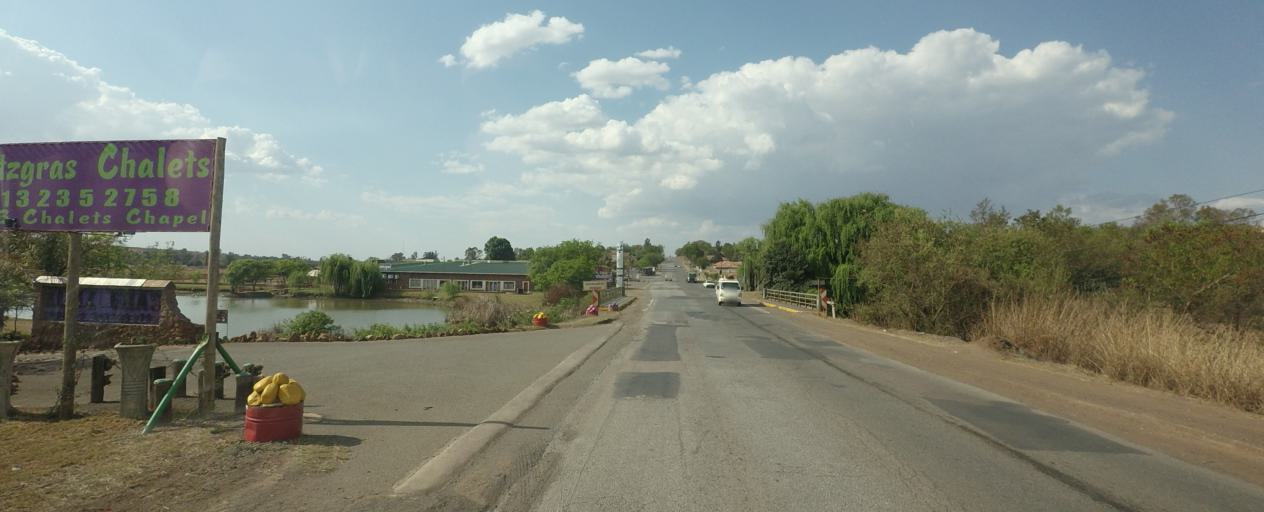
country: ZA
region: Mpumalanga
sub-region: Ehlanzeni District
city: Lydenburg
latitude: -25.1133
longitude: 30.4474
